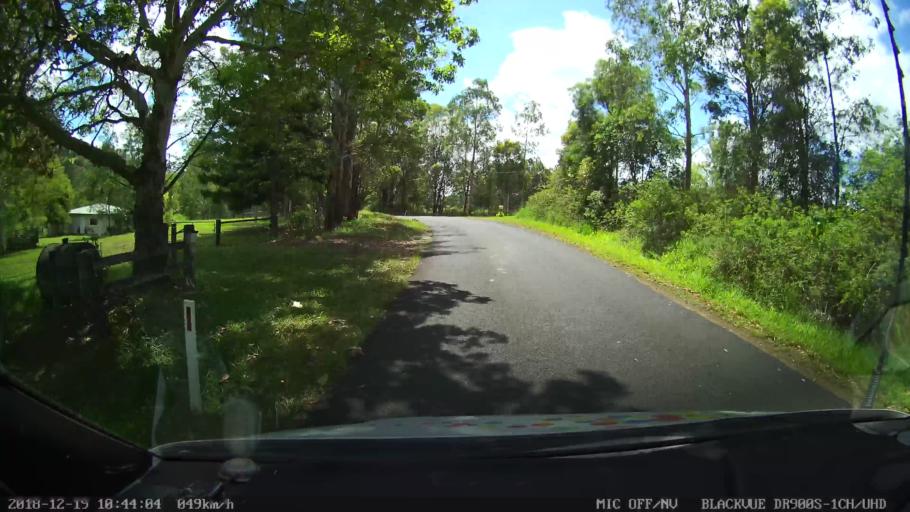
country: AU
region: New South Wales
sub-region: Lismore Municipality
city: Nimbin
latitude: -28.5963
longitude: 153.1776
